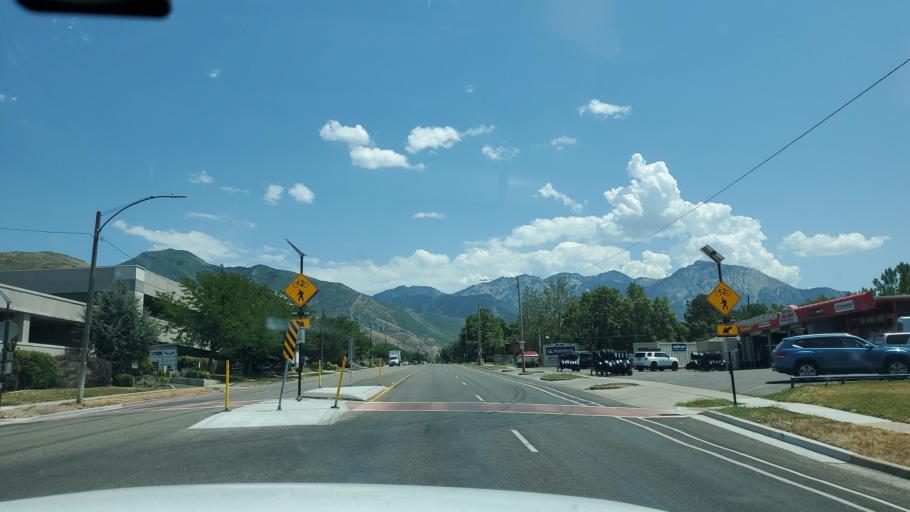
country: US
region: Utah
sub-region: Salt Lake County
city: Canyon Rim
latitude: 40.7229
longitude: -111.8209
